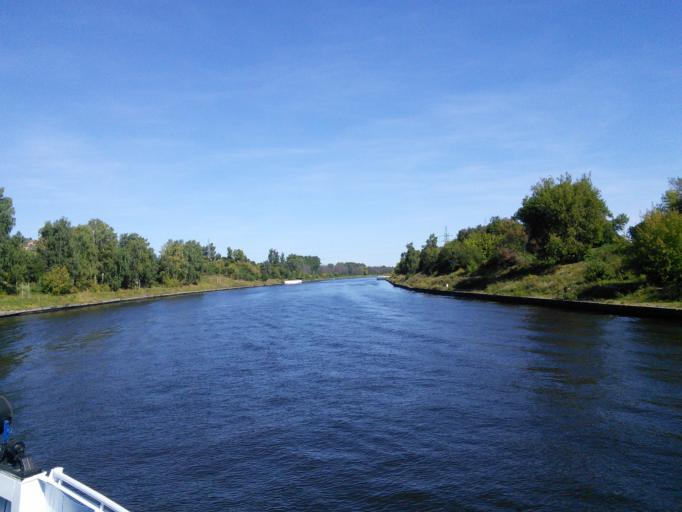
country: RU
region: Moskovskaya
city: Dolgoprudnyy
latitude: 55.9456
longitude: 37.4792
